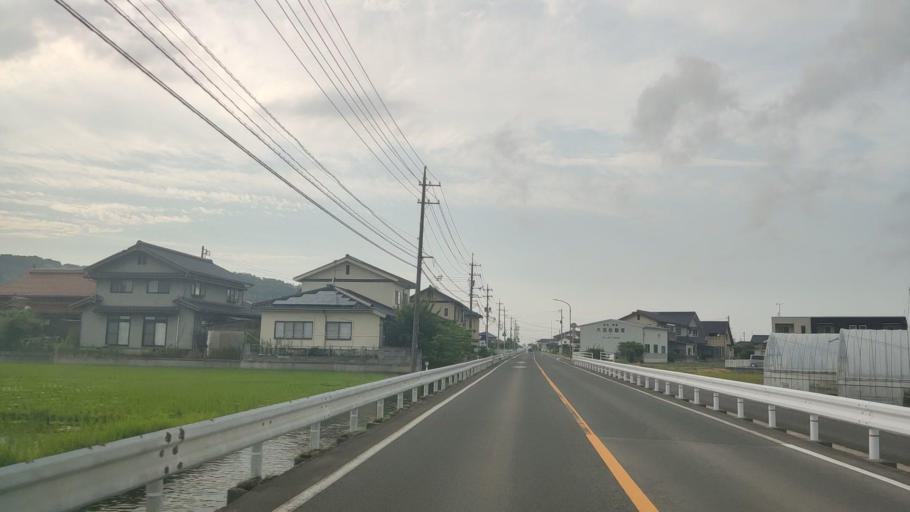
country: JP
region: Tottori
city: Kurayoshi
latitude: 35.4604
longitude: 133.8351
